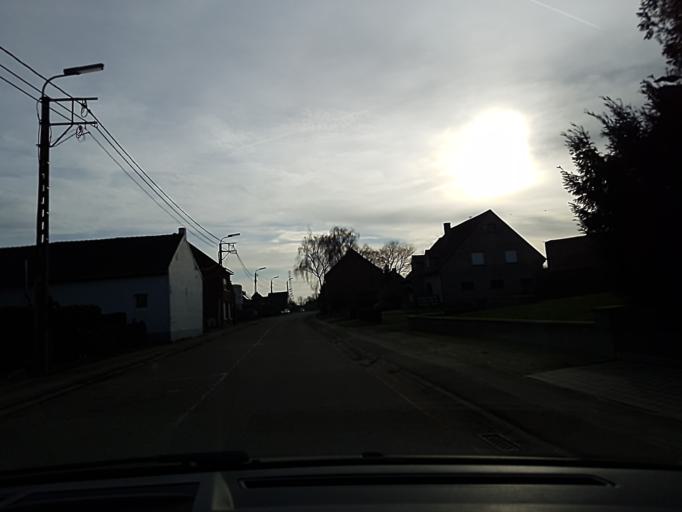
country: BE
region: Flanders
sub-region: Provincie Vlaams-Brabant
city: Rotselaar
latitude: 50.9479
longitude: 4.6796
